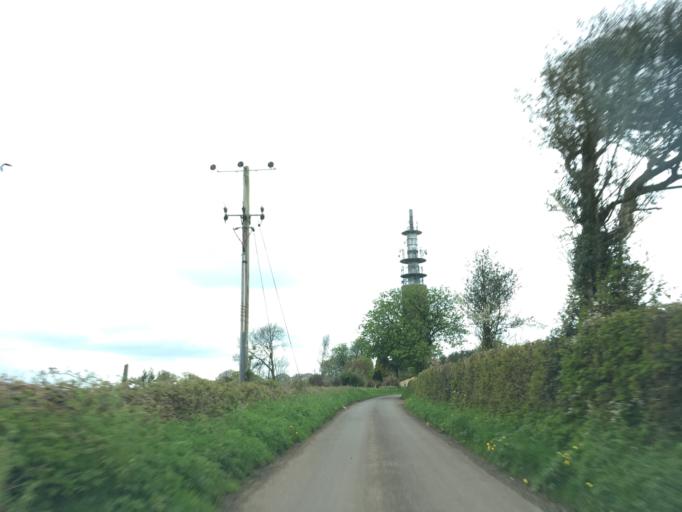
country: GB
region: England
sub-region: Gloucestershire
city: Wotton-under-Edge
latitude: 51.6472
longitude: -2.3037
